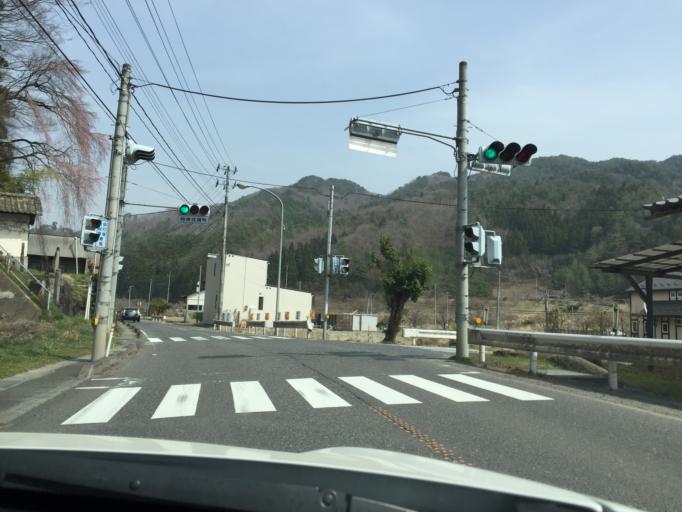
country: JP
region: Fukushima
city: Ishikawa
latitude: 37.0833
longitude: 140.5202
